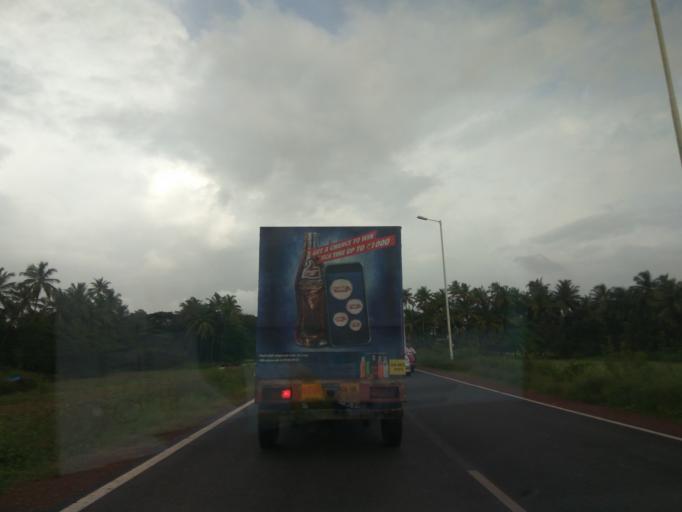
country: IN
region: Goa
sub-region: North Goa
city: Goa Velha
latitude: 15.4369
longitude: 73.8822
